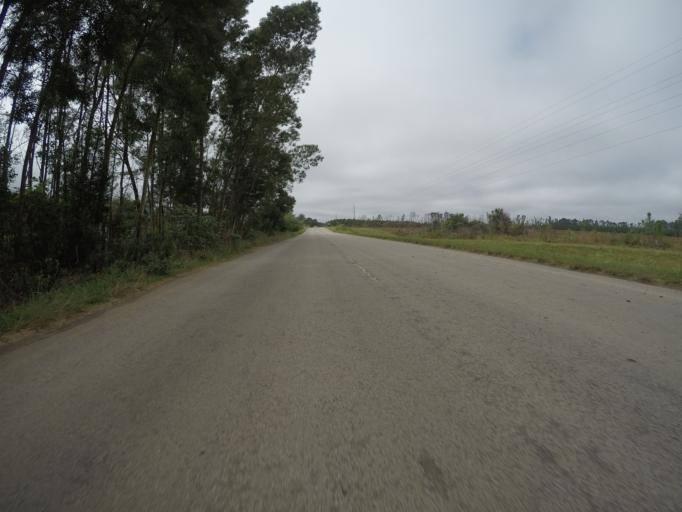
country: ZA
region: Eastern Cape
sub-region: Cacadu District Municipality
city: Kareedouw
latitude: -33.9965
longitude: 24.1392
